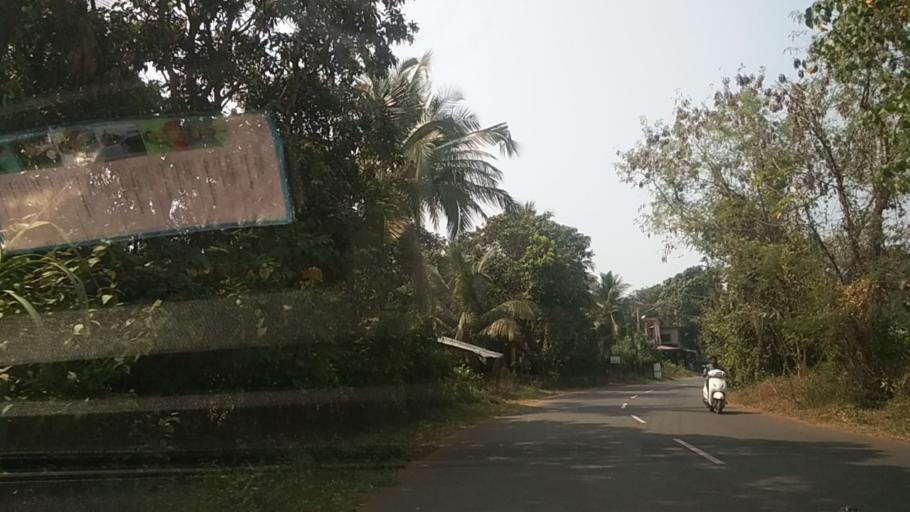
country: IN
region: Goa
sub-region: North Goa
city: Morjim
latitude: 15.6619
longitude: 73.7317
